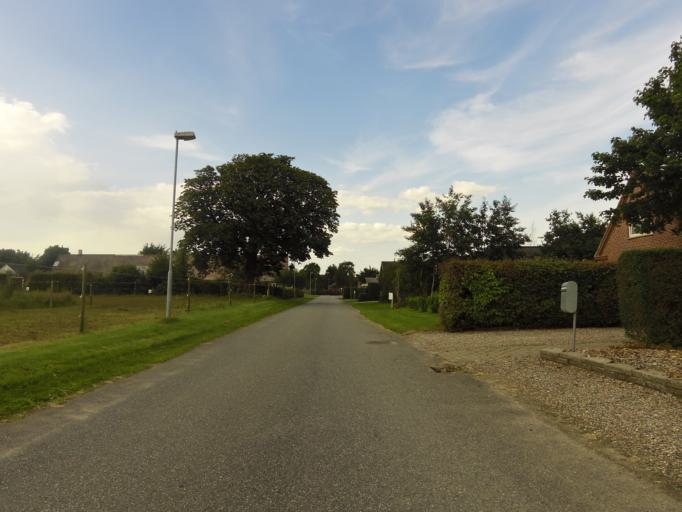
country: DK
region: South Denmark
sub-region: Tonder Kommune
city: Logumkloster
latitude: 55.1490
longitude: 8.9570
